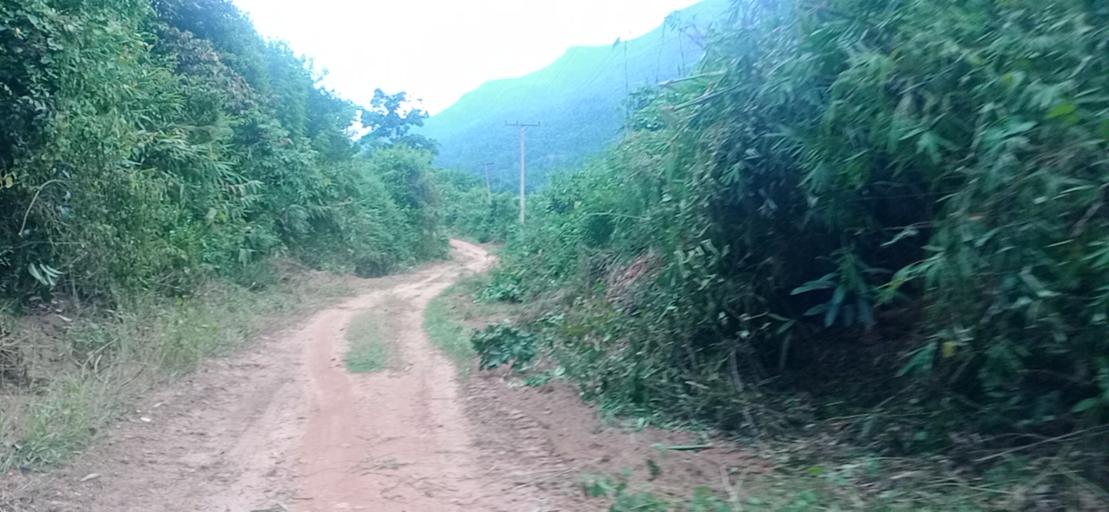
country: TH
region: Changwat Bueng Kan
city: Pak Khat
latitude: 18.5600
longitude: 103.2293
